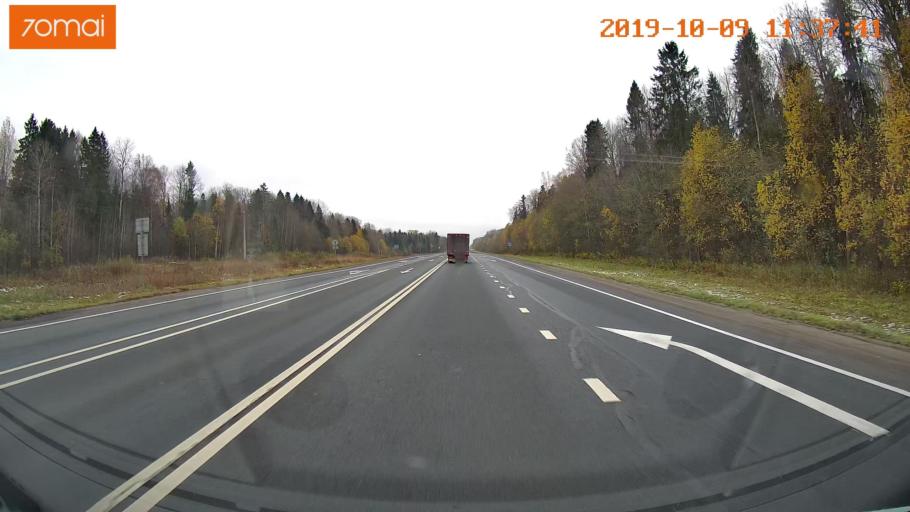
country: RU
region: Vologda
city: Gryazovets
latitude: 58.9764
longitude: 40.1488
